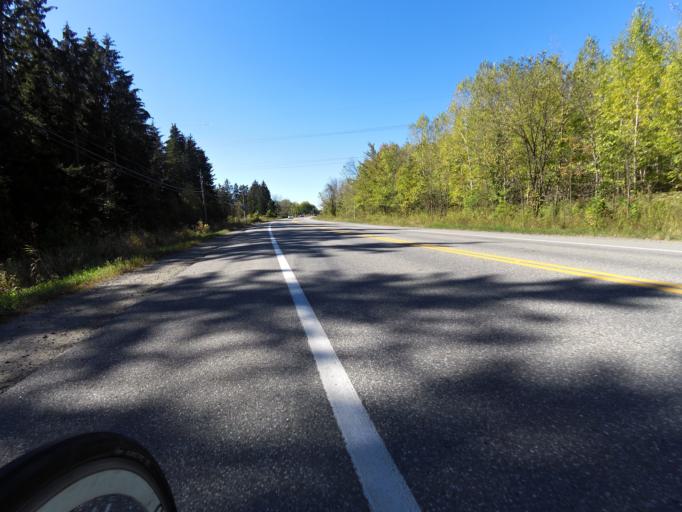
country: CA
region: Ontario
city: Clarence-Rockland
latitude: 45.5400
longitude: -75.4357
